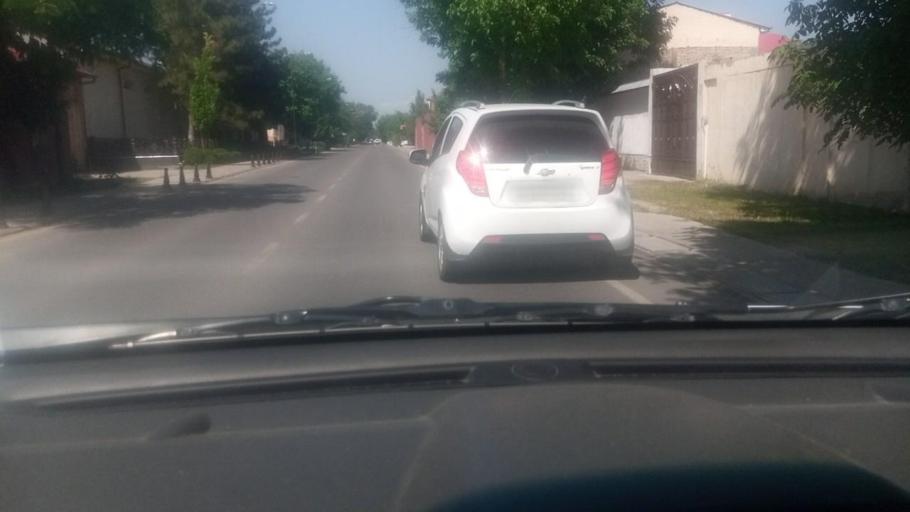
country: UZ
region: Toshkent
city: Salor
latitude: 41.3306
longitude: 69.3562
